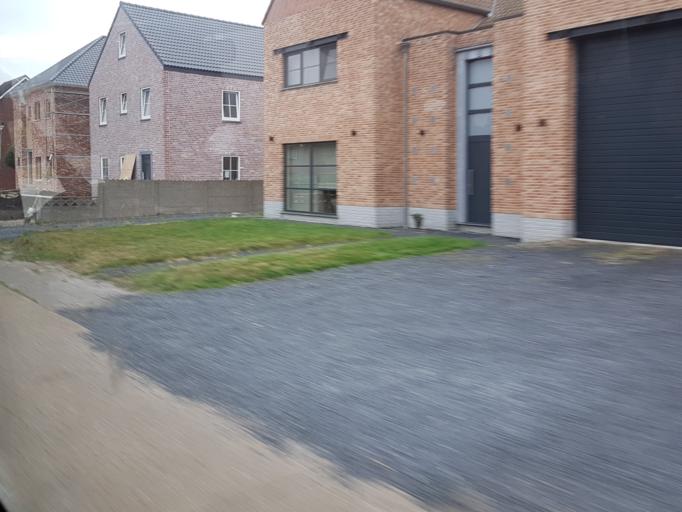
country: BE
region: Flanders
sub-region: Provincie Limburg
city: Overpelt
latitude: 51.2137
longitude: 5.3838
